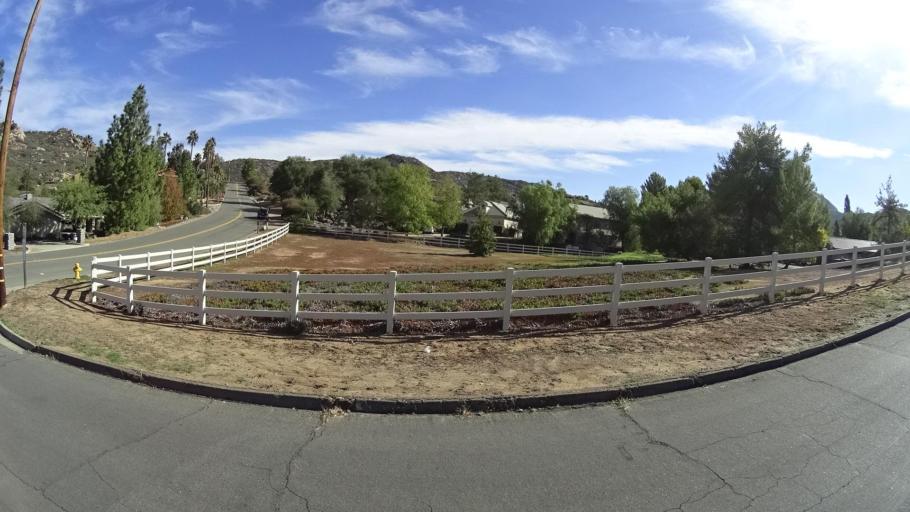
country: US
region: California
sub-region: San Diego County
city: Alpine
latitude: 32.8133
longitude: -116.7328
